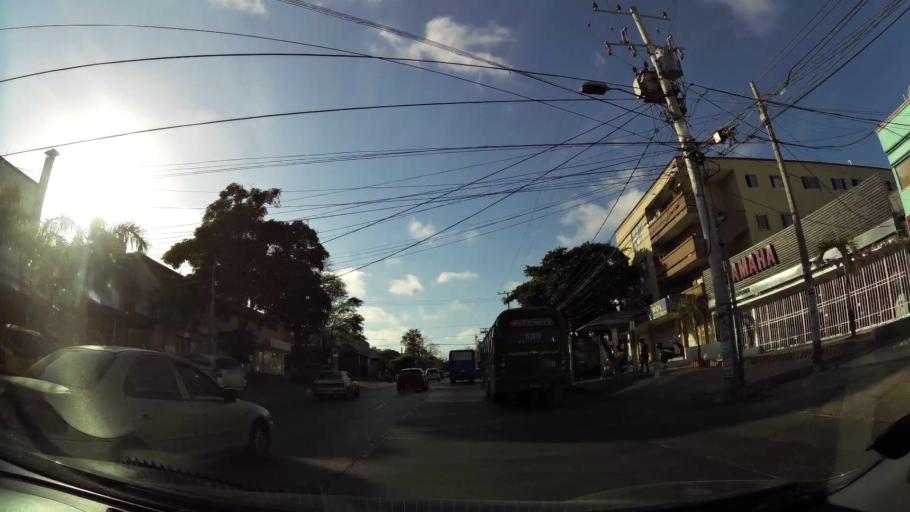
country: CO
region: Atlantico
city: Barranquilla
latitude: 10.9898
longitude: -74.8038
